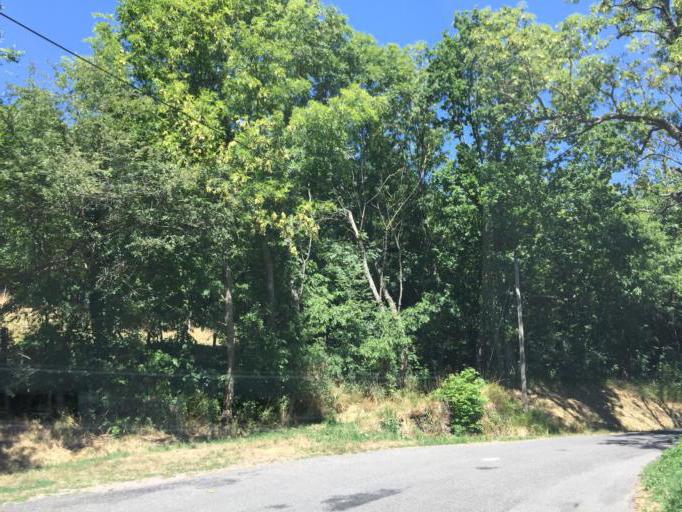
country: FR
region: Rhone-Alpes
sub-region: Departement de la Loire
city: Saint-Jean-Bonnefonds
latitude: 45.4657
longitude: 4.4576
